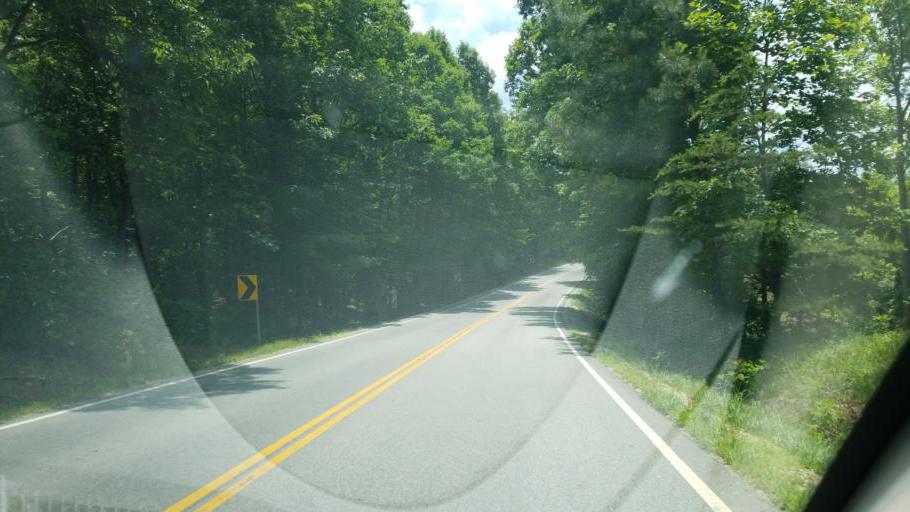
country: US
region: Virginia
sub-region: Appomattox County
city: Appomattox
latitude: 37.5554
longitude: -78.8378
